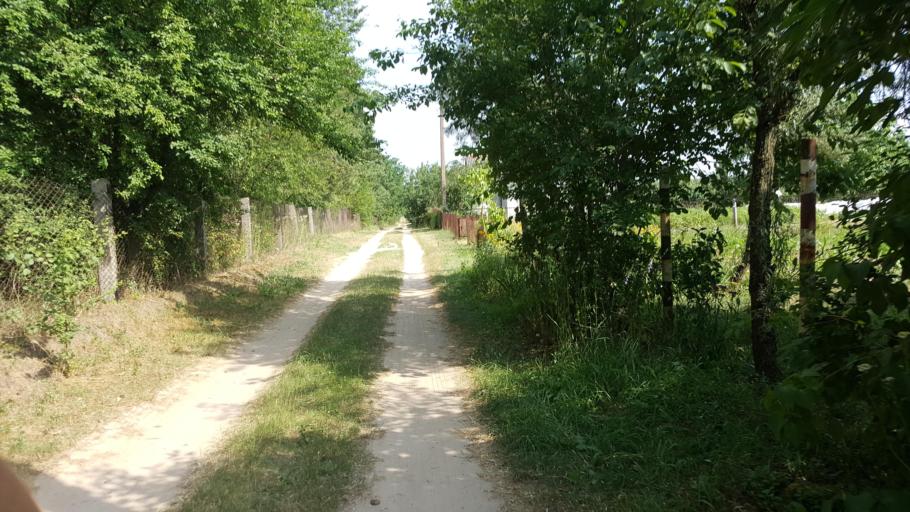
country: BY
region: Brest
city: Kamyanyets
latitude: 52.3702
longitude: 23.8034
